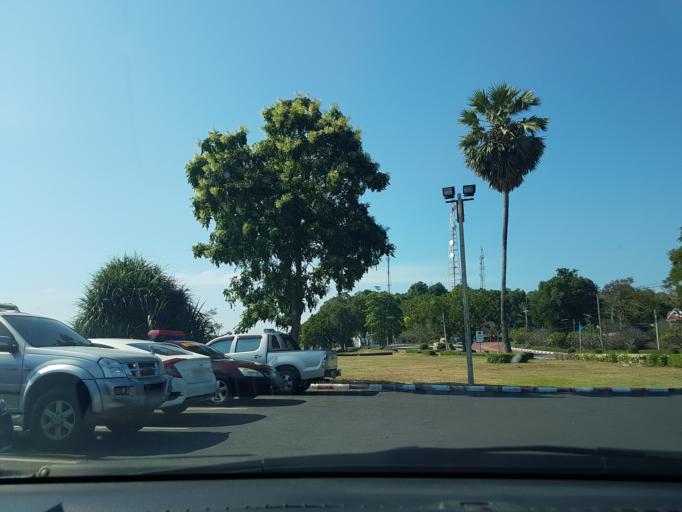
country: TH
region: Chon Buri
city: Sattahip
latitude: 12.6584
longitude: 100.8899
